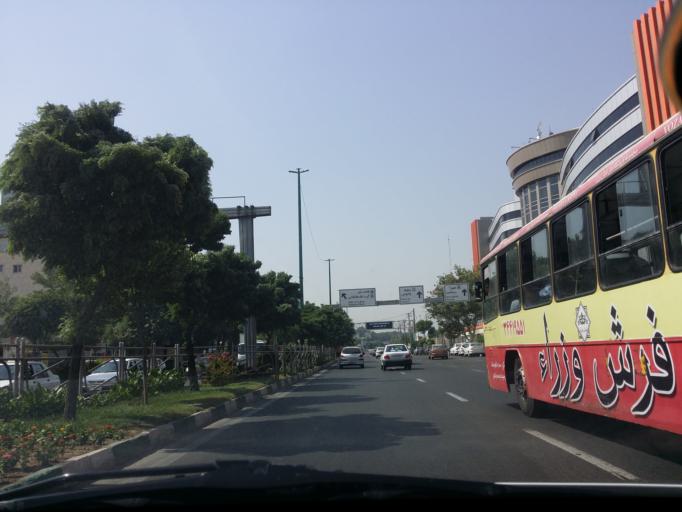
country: IR
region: Alborz
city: Karaj
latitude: 35.7953
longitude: 51.0021
